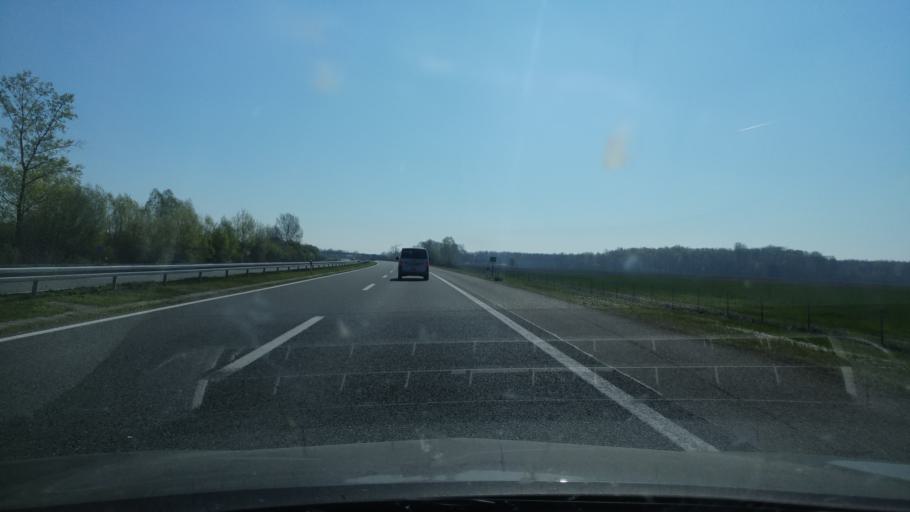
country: HR
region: Brodsko-Posavska
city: Garcin
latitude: 45.1592
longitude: 18.1817
